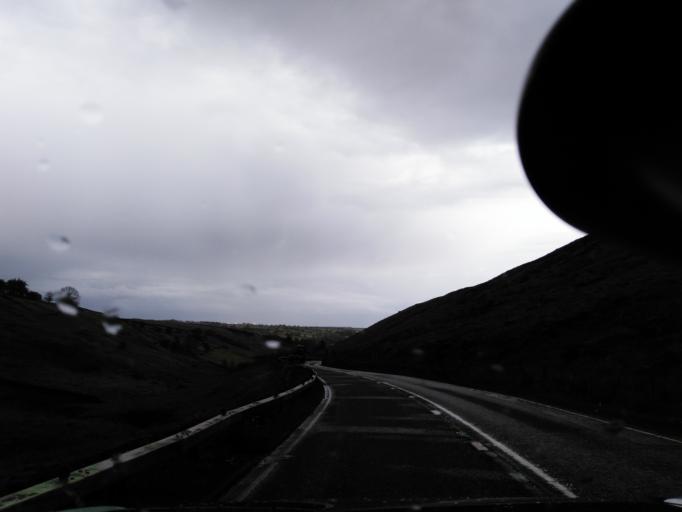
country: GB
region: England
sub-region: Bradford
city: Ilkley
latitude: 53.9933
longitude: -1.7887
